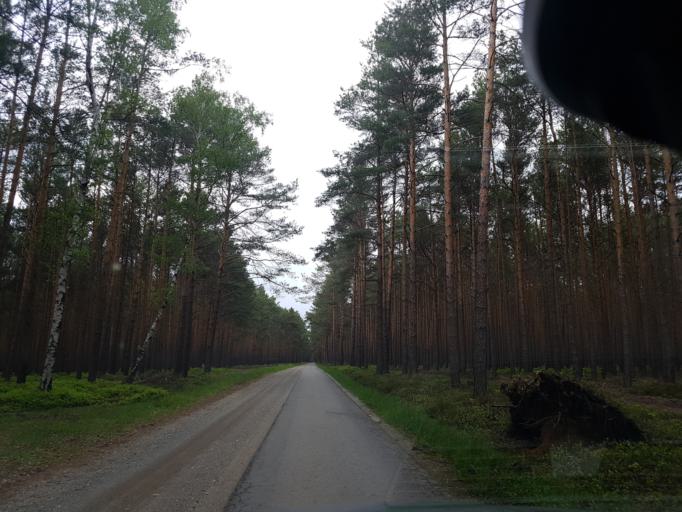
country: DE
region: Brandenburg
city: Crinitz
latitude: 51.6927
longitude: 13.7761
